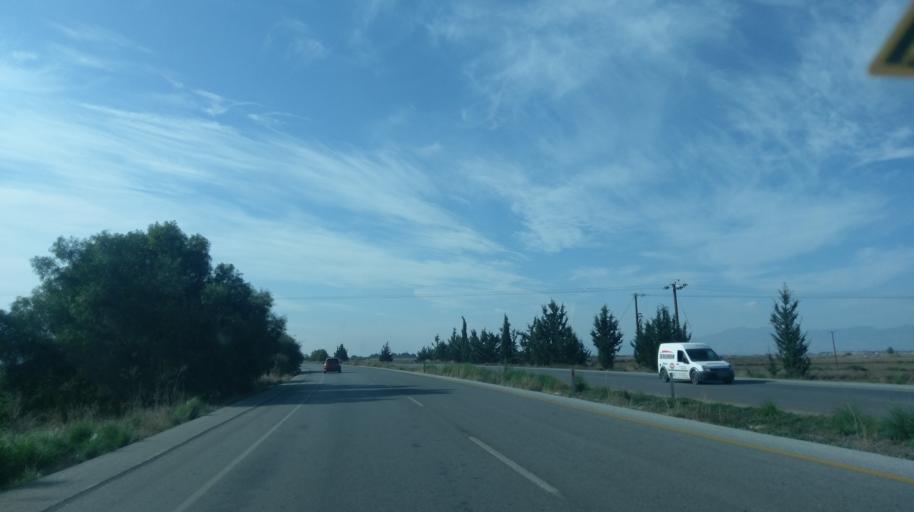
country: CY
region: Ammochostos
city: Lefkonoiko
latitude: 35.1787
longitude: 33.7484
